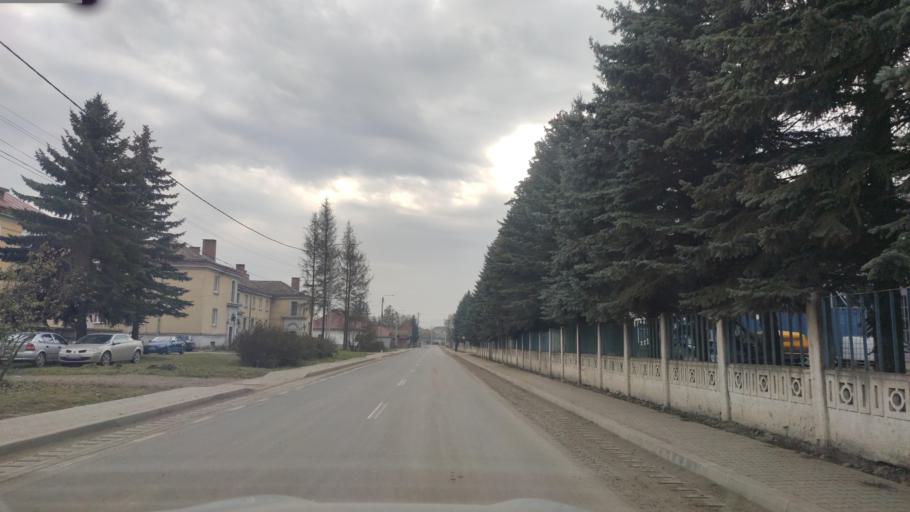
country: RO
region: Harghita
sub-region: Comuna Remetea
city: Remetea
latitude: 46.8134
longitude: 25.4599
